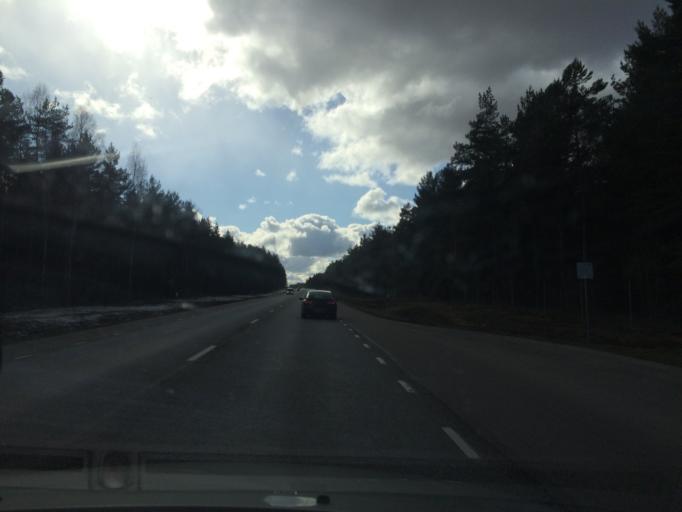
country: SE
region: Vaestra Goetaland
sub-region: Gotene Kommun
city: Goetene
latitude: 58.6133
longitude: 13.6540
